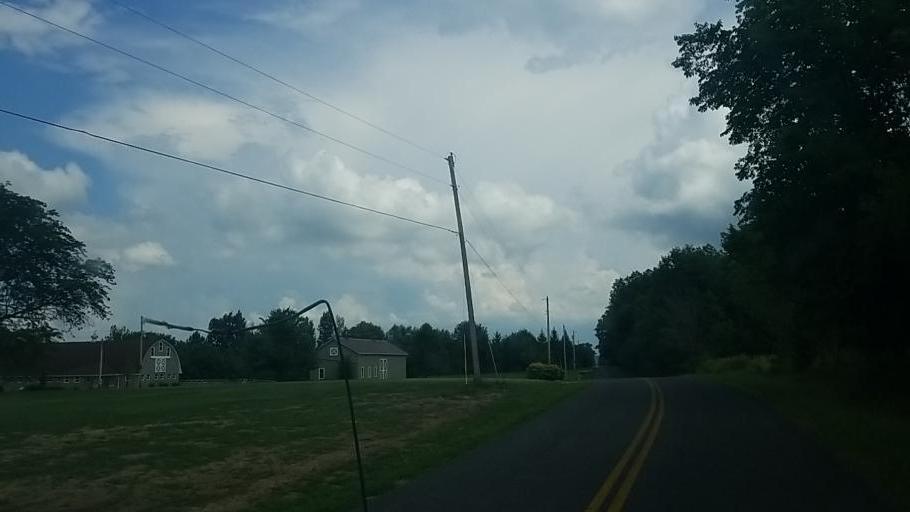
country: US
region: Ohio
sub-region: Medina County
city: Lodi
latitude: 41.1424
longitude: -81.9805
